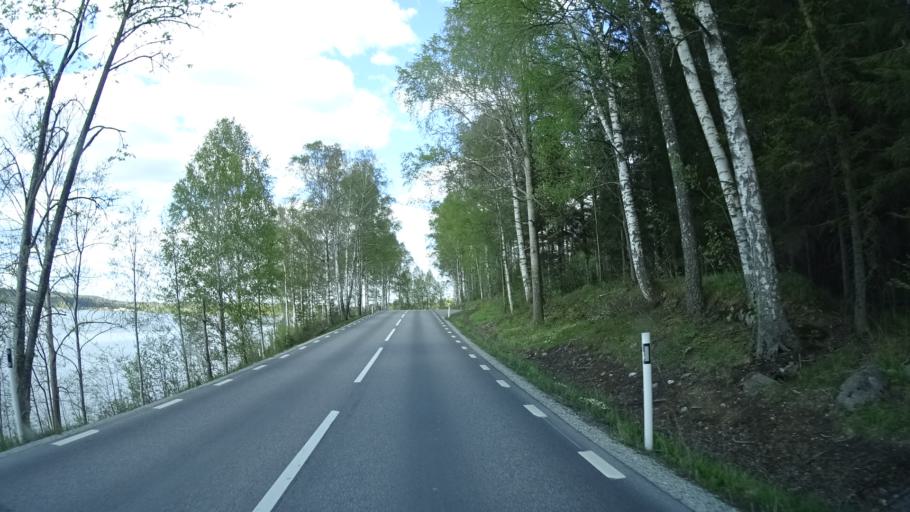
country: SE
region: OErebro
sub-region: Nora Kommun
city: As
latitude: 59.4955
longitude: 14.9472
